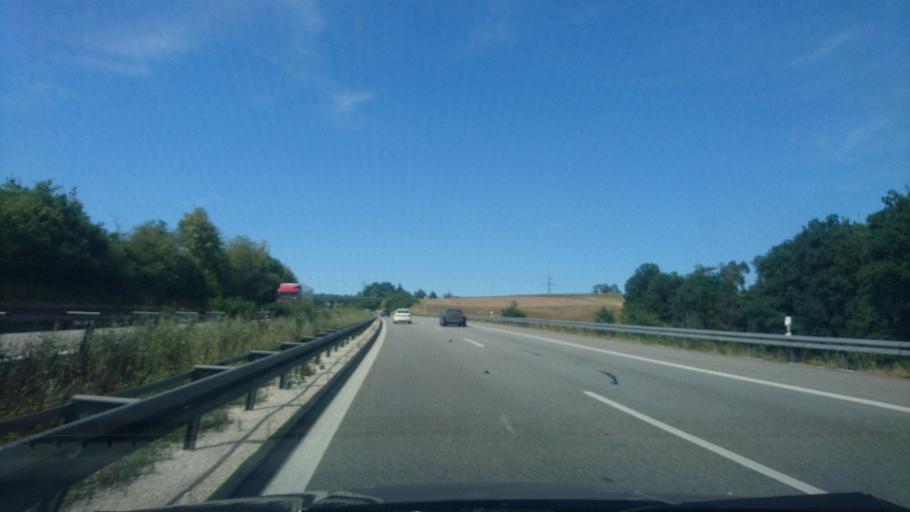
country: DE
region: Bavaria
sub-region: Upper Palatinate
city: Maxhutte-Haidhof
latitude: 49.1846
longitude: 12.1238
